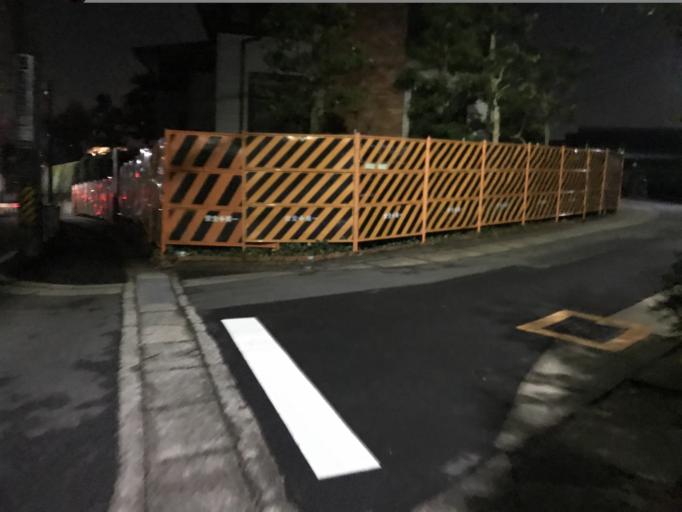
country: JP
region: Aichi
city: Nagoya-shi
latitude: 35.1351
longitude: 136.9680
